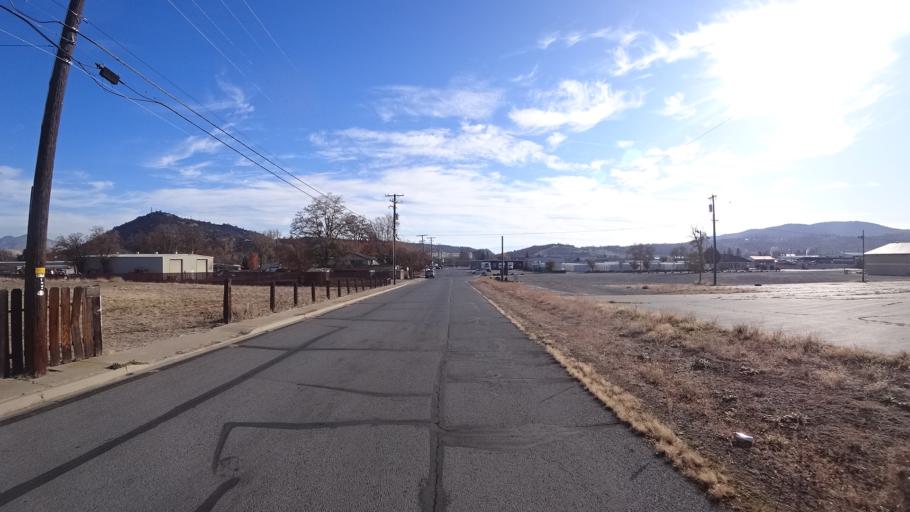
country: US
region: California
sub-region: Siskiyou County
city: Yreka
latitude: 41.7158
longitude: -122.6440
